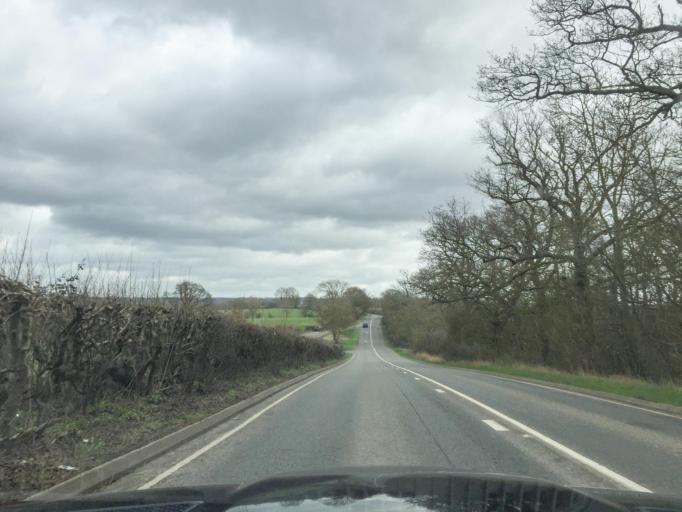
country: GB
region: England
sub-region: Warwickshire
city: Wellesbourne Mountford
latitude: 52.1251
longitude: -1.5617
